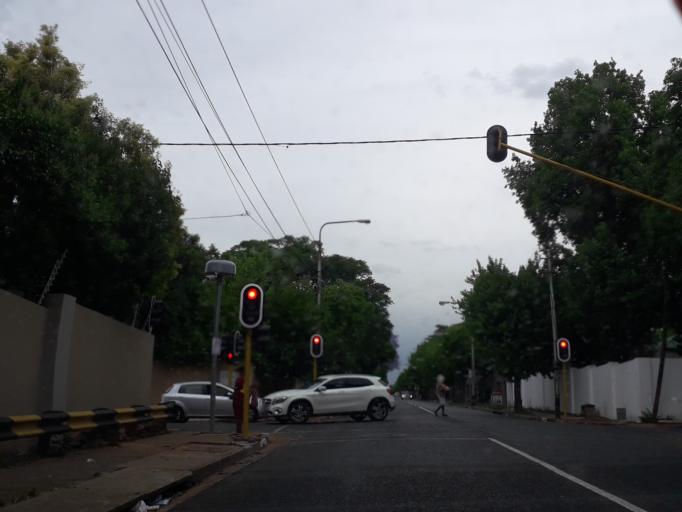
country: ZA
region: Gauteng
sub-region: City of Johannesburg Metropolitan Municipality
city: Johannesburg
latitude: -26.1500
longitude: 28.0773
